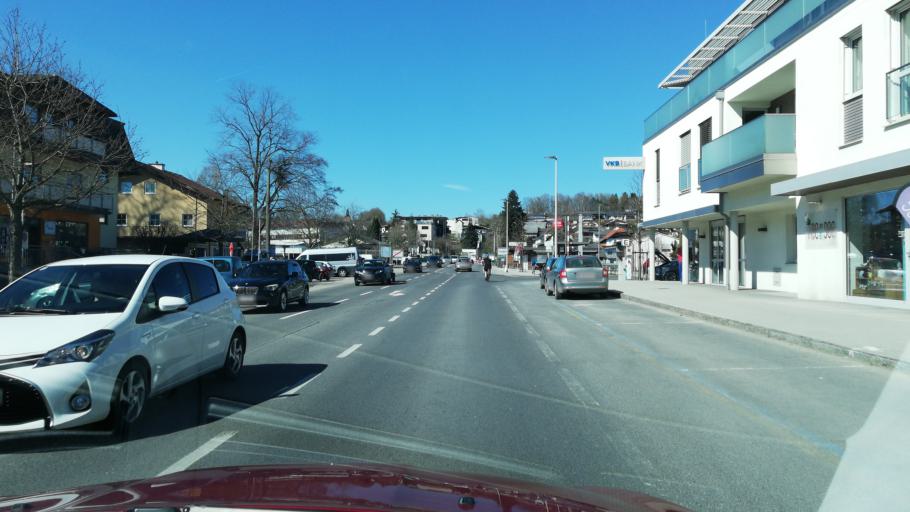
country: AT
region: Upper Austria
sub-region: Politischer Bezirk Vocklabruck
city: Seewalchen
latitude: 47.9477
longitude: 13.5952
